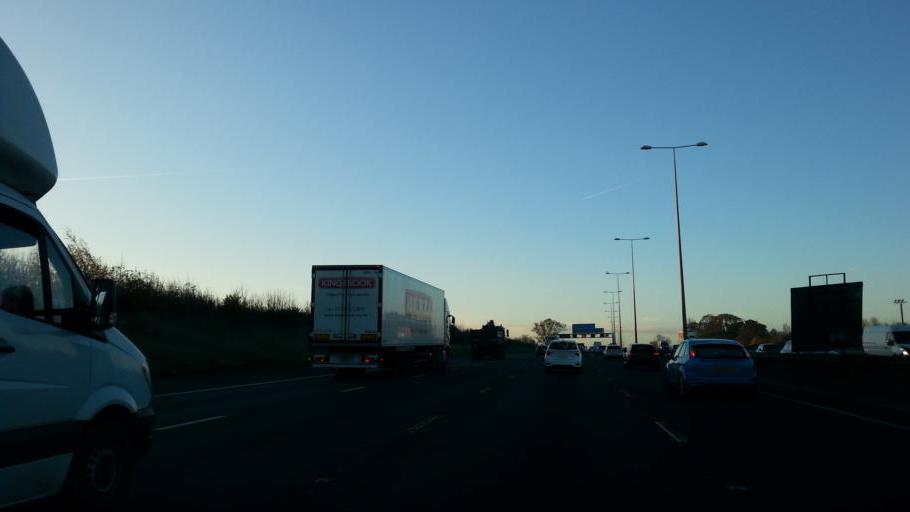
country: GB
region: England
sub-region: Hertfordshire
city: Redbourn
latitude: 51.7822
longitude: -0.4111
